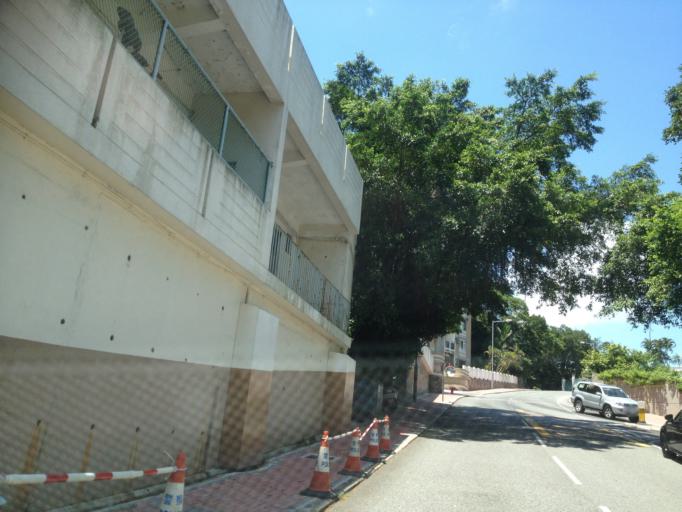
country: HK
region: Central and Western
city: Central
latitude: 22.2667
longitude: 114.1619
